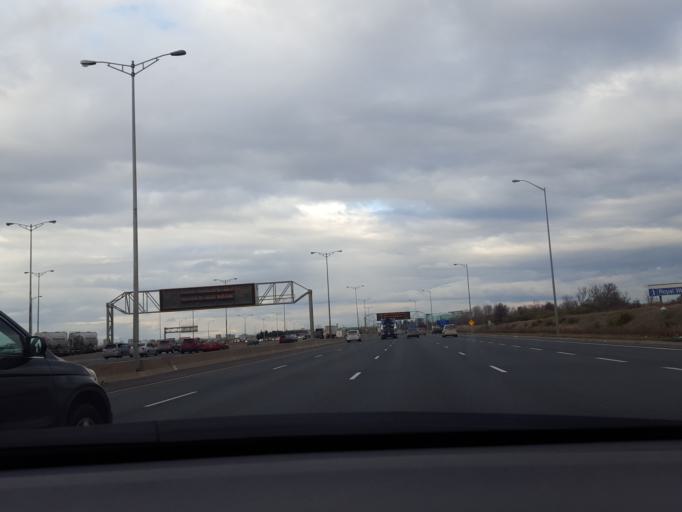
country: CA
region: Ontario
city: Etobicoke
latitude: 43.6507
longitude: -79.6303
